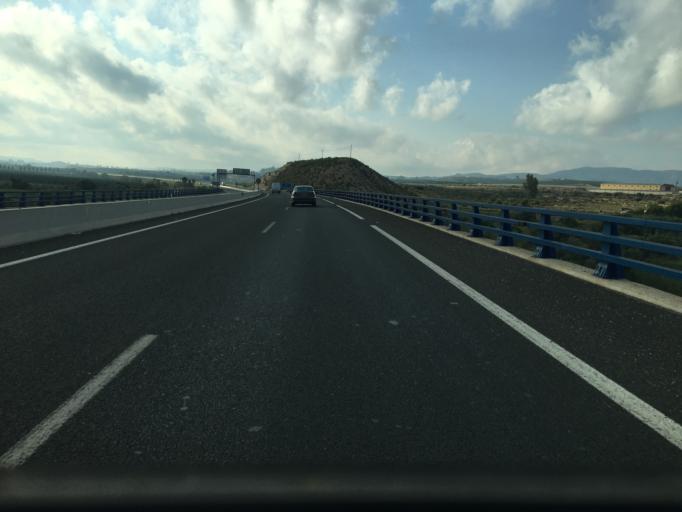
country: ES
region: Murcia
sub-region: Murcia
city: Beniel
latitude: 37.9980
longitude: -1.0072
